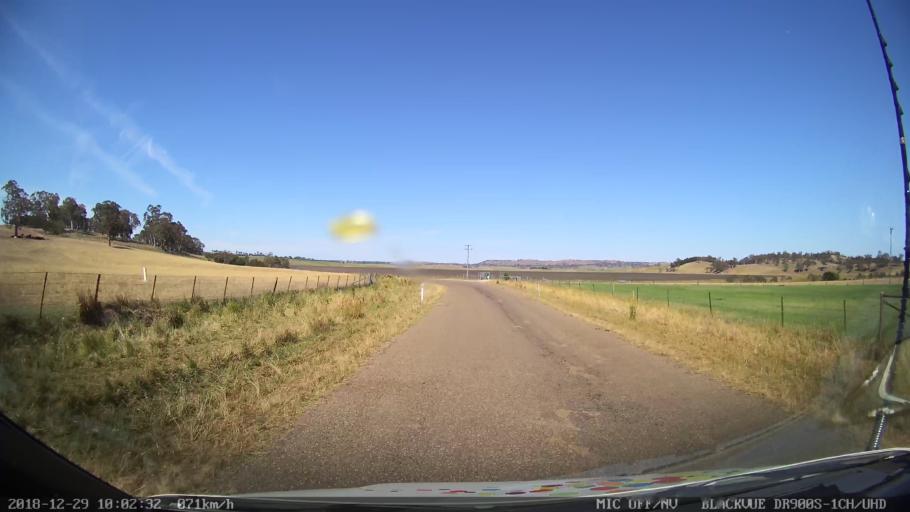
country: AU
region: New South Wales
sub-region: Goulburn Mulwaree
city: Goulburn
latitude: -34.8020
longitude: 149.4631
